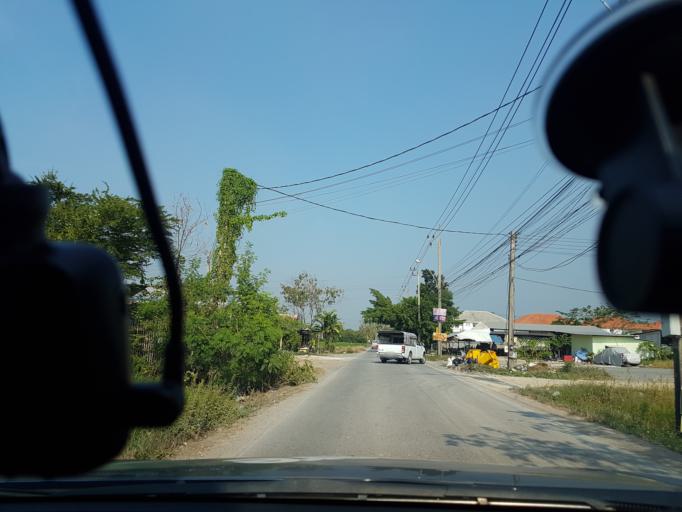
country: TH
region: Pathum Thani
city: Lam Luk Ka
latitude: 13.9080
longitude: 100.7019
